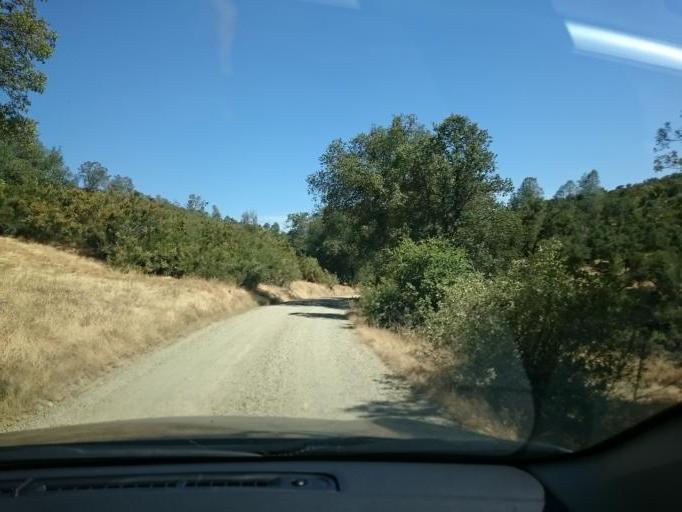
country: US
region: California
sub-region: Calaveras County
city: Rancho Calaveras
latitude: 38.0948
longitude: -120.7604
